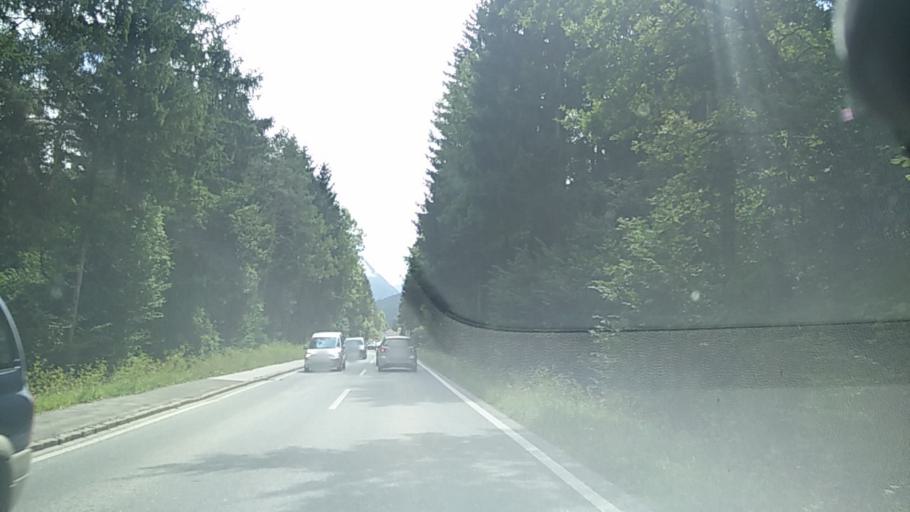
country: AT
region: Carinthia
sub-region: Politischer Bezirk Klagenfurt Land
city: Ferlach
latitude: 46.5318
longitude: 14.2848
